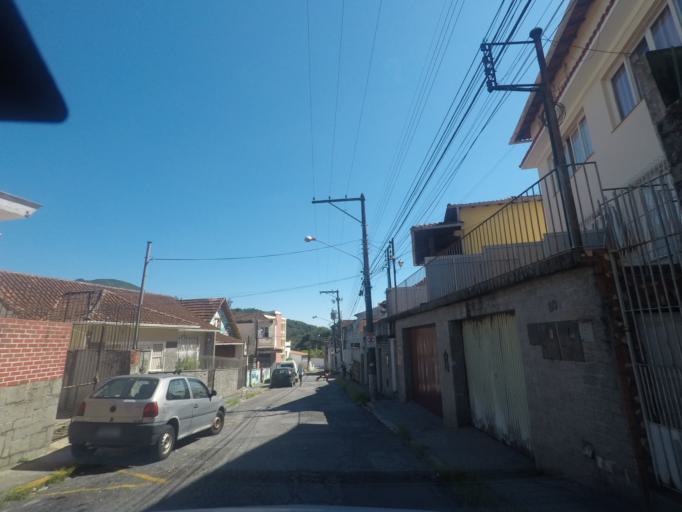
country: BR
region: Rio de Janeiro
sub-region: Petropolis
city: Petropolis
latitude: -22.5125
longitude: -43.1889
